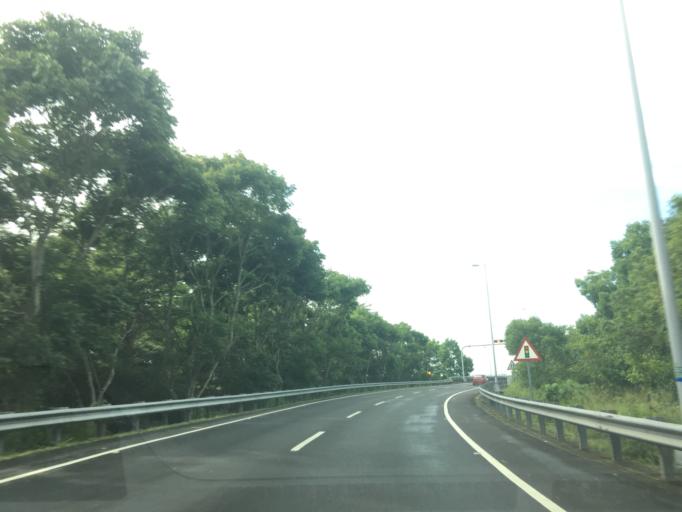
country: TW
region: Taiwan
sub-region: Chiayi
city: Jiayi Shi
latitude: 23.4519
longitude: 120.4868
